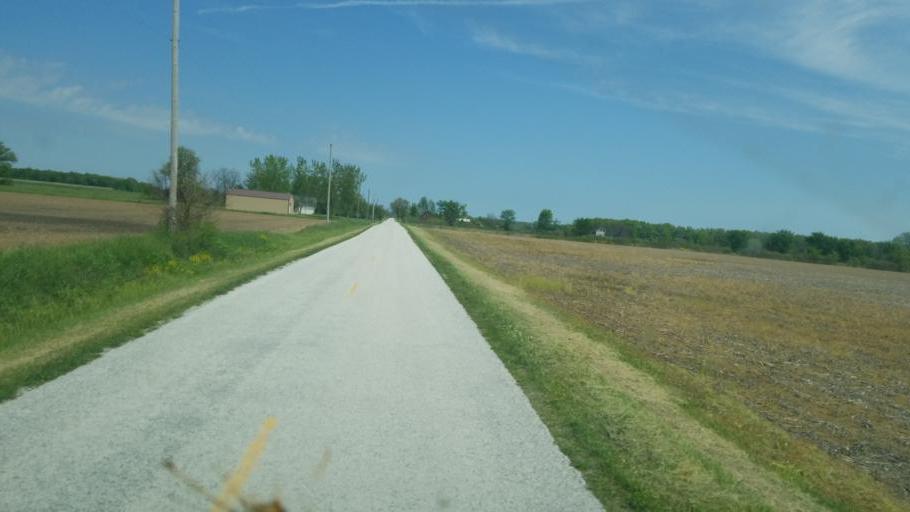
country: US
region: Ohio
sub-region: Ottawa County
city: Oak Harbor
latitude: 41.4786
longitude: -83.2019
